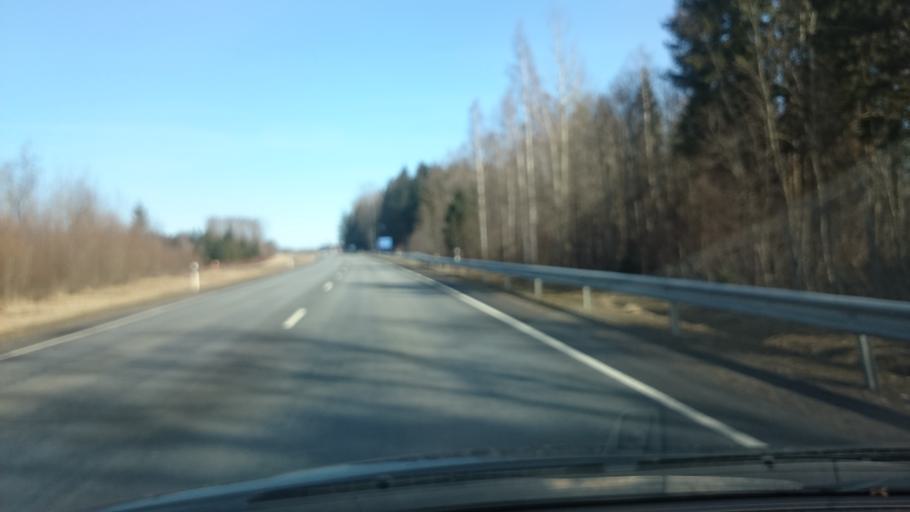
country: EE
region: Paernumaa
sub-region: Vaendra vald (alev)
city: Vandra
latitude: 58.6496
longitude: 24.9922
